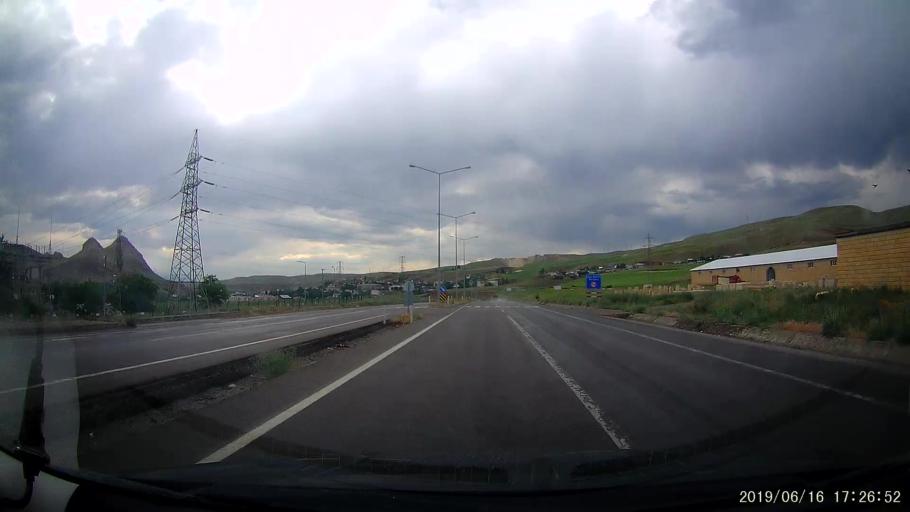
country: TR
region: Erzincan
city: Tercan
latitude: 39.7725
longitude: 40.4037
